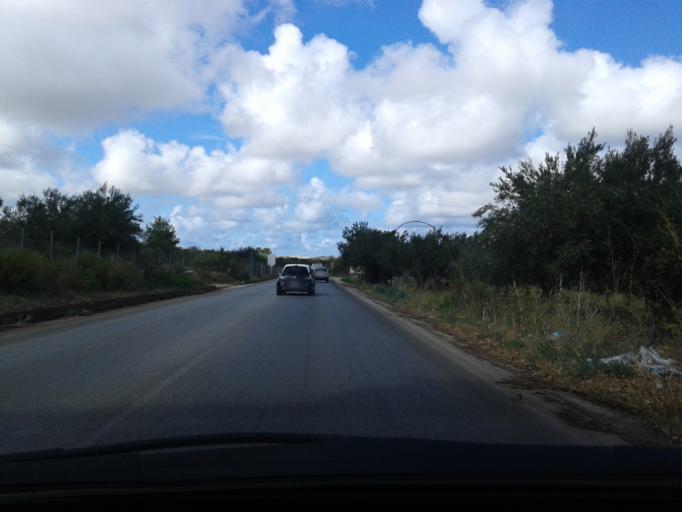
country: IT
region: Sicily
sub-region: Trapani
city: Castelluzzo
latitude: 38.0754
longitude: 12.7368
